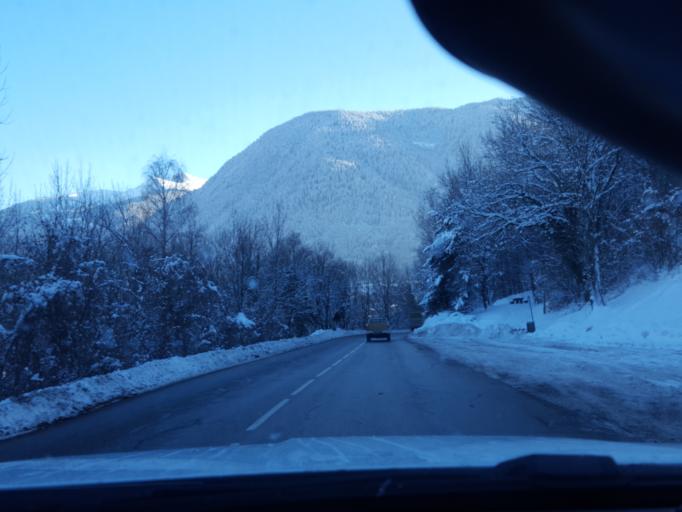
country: FR
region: Rhone-Alpes
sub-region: Departement de la Savoie
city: Salins-les-Thermes
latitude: 45.4733
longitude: 6.5231
